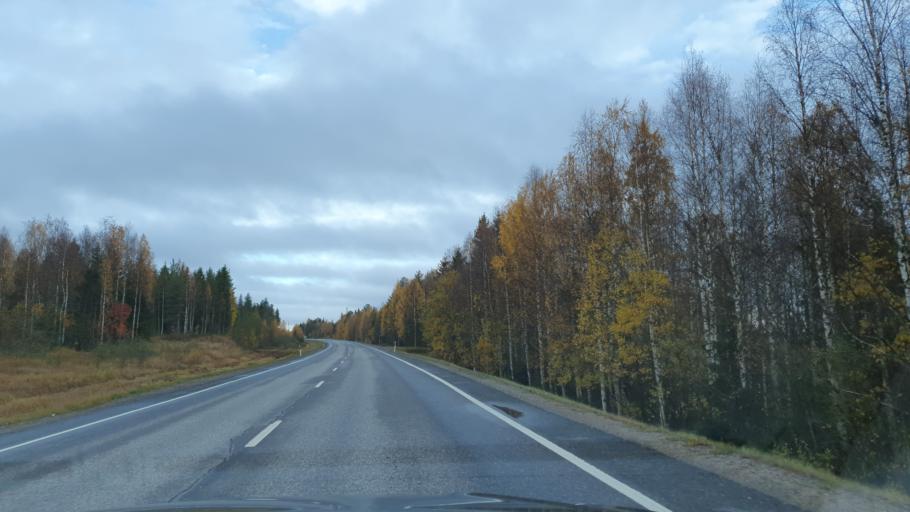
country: FI
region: Lapland
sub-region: Rovaniemi
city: Rovaniemi
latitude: 66.5735
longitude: 25.6319
